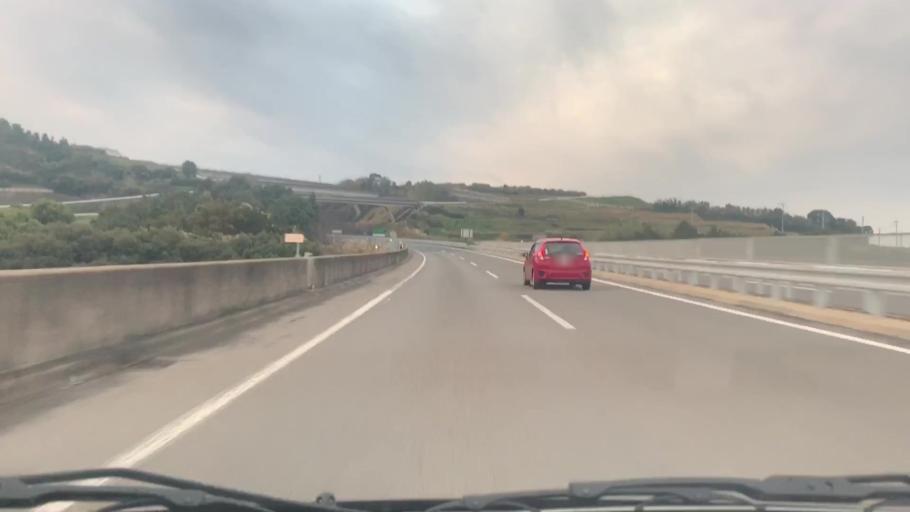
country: JP
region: Nagasaki
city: Omura
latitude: 33.0022
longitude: 129.9522
